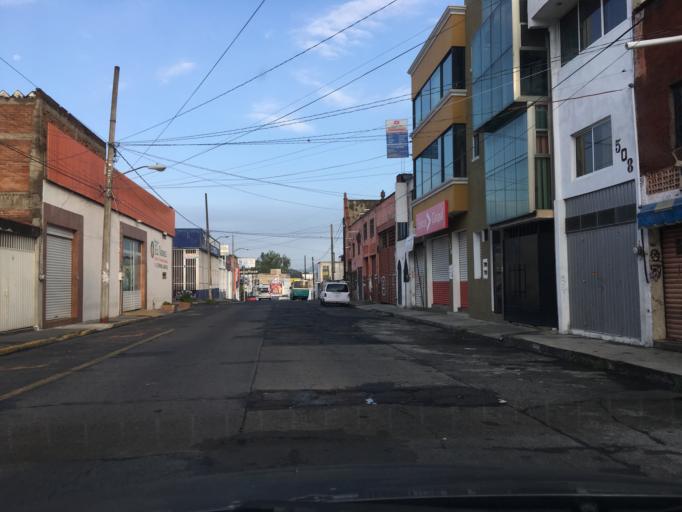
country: MX
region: Michoacan
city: Morelia
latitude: 19.7008
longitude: -101.2122
